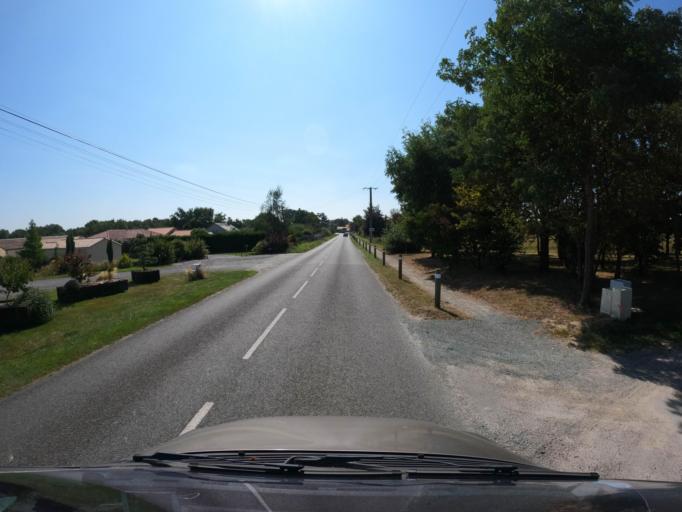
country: FR
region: Pays de la Loire
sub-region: Departement de la Loire-Atlantique
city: Montbert
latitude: 47.0645
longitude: -1.4958
